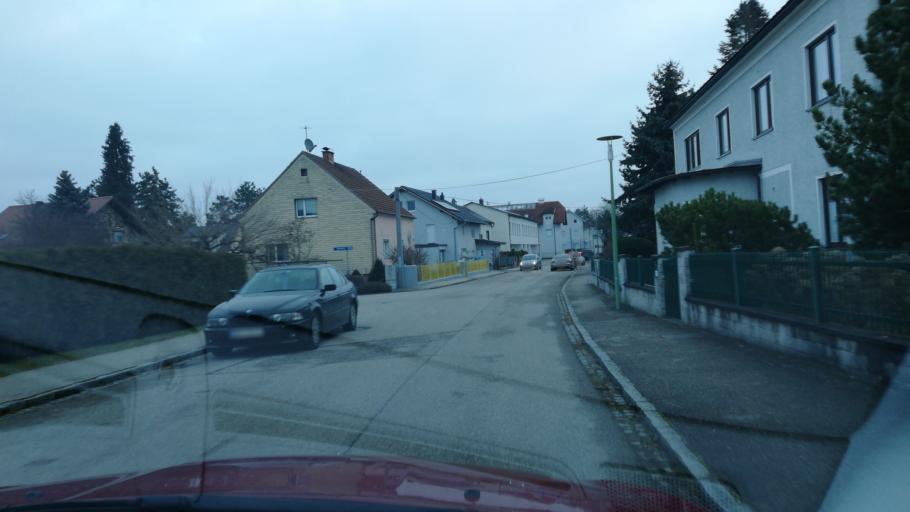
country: AT
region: Upper Austria
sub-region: Wels Stadt
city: Wels
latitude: 48.1690
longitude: 14.0407
